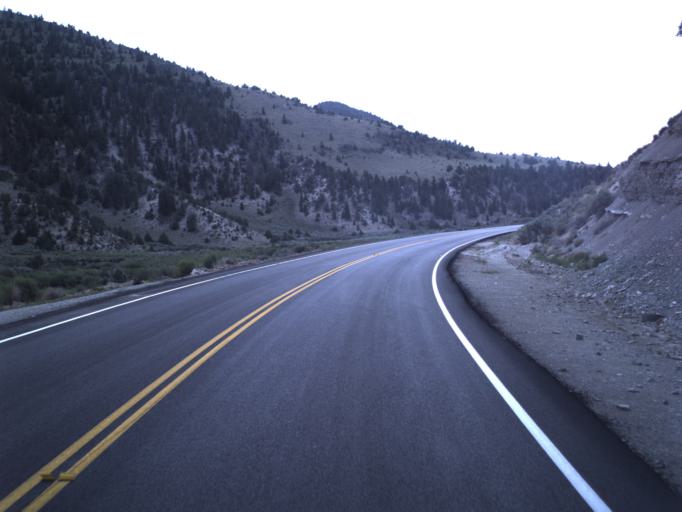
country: US
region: Utah
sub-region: Duchesne County
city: Duchesne
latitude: 39.9755
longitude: -110.6195
